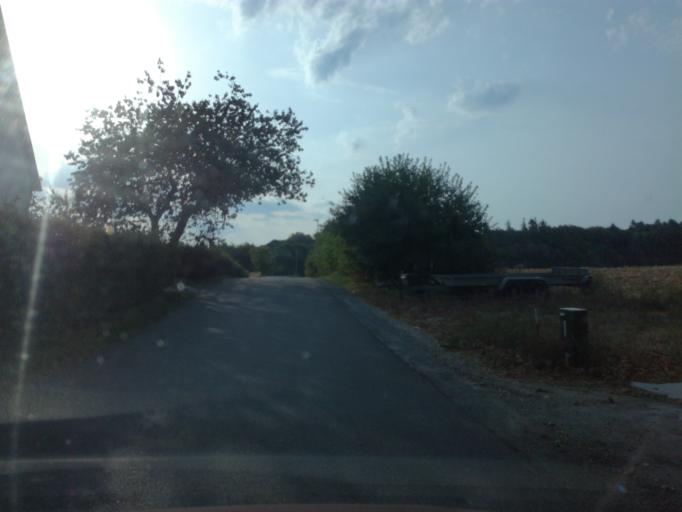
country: DK
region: South Denmark
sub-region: Vejle Kommune
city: Vejle
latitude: 55.6486
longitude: 9.5441
